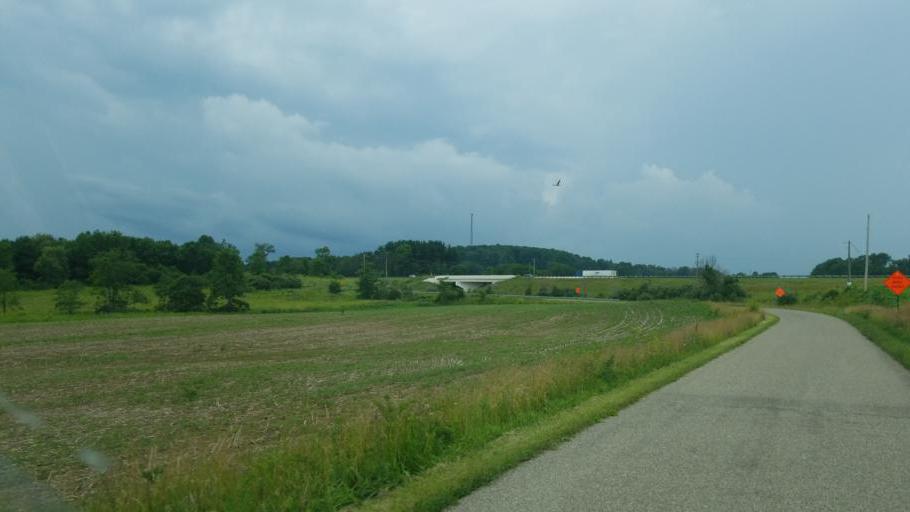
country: US
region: Ohio
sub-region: Sandusky County
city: Bellville
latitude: 40.6028
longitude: -82.5820
